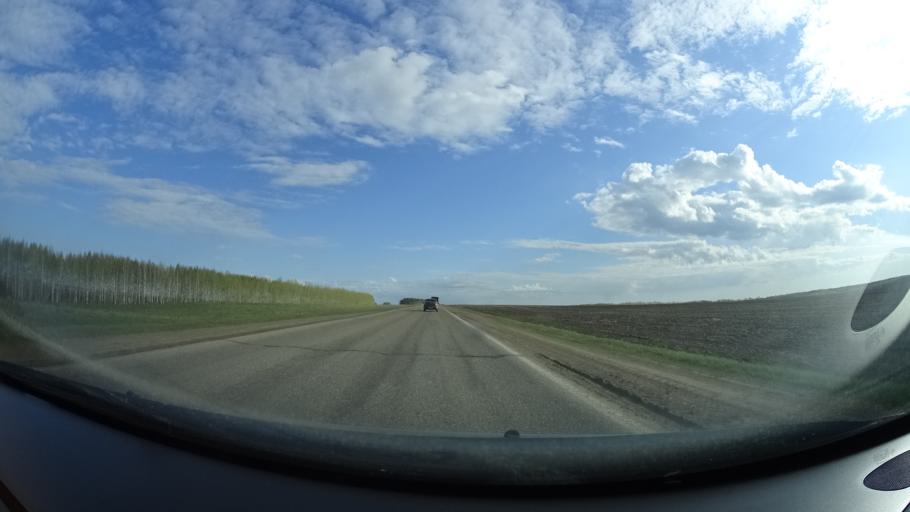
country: RU
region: Bashkortostan
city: Blagoveshchensk
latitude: 55.1448
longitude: 55.8500
